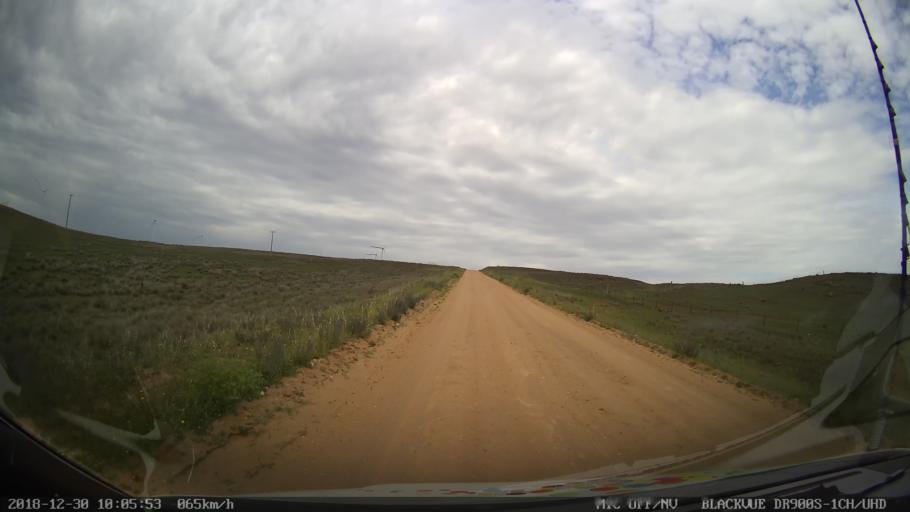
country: AU
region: New South Wales
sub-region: Cooma-Monaro
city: Cooma
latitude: -36.5291
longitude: 149.1331
